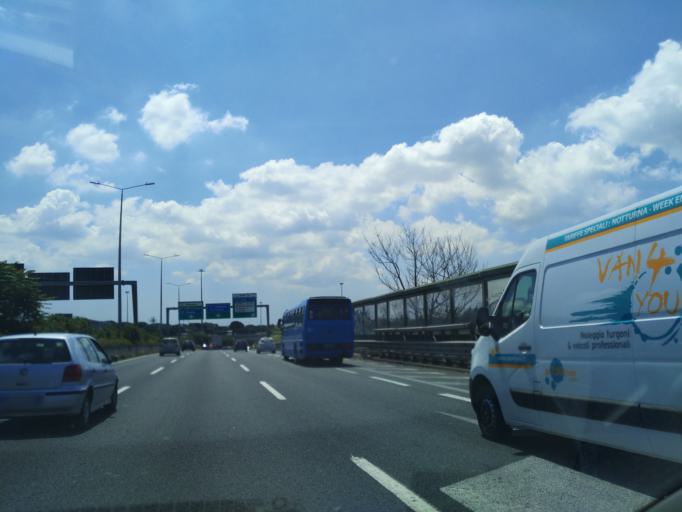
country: IT
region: Latium
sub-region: Citta metropolitana di Roma Capitale
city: Ciampino
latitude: 41.8167
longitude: 12.5764
